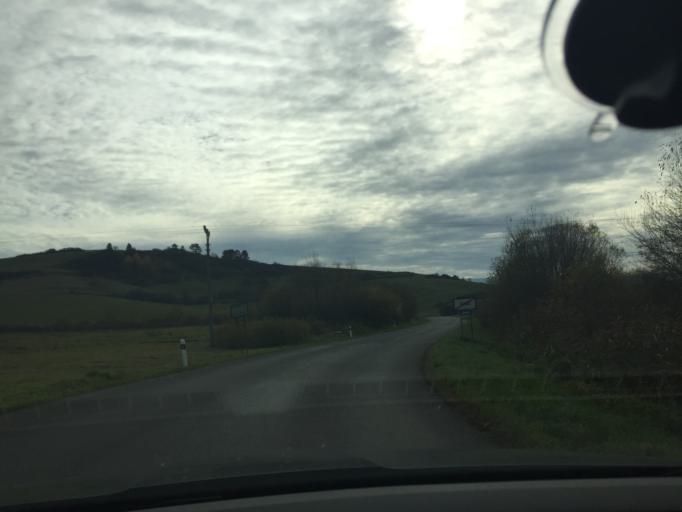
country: SK
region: Presovsky
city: Spisske Podhradie
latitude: 48.9775
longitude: 20.7934
